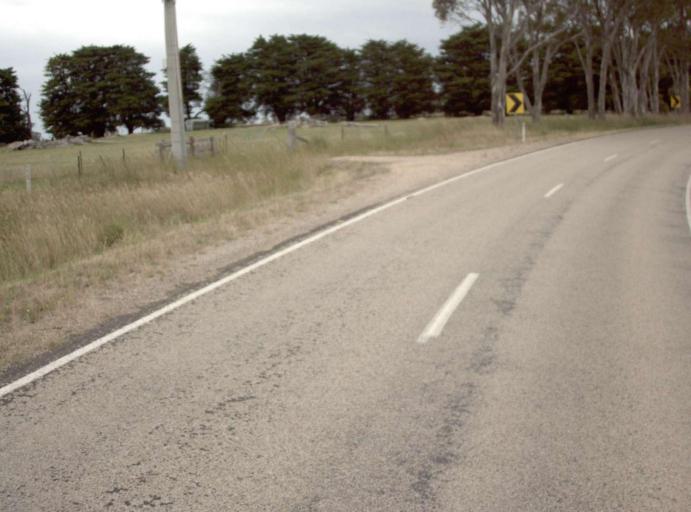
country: AU
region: Victoria
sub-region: East Gippsland
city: Bairnsdale
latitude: -37.9325
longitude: 147.5372
